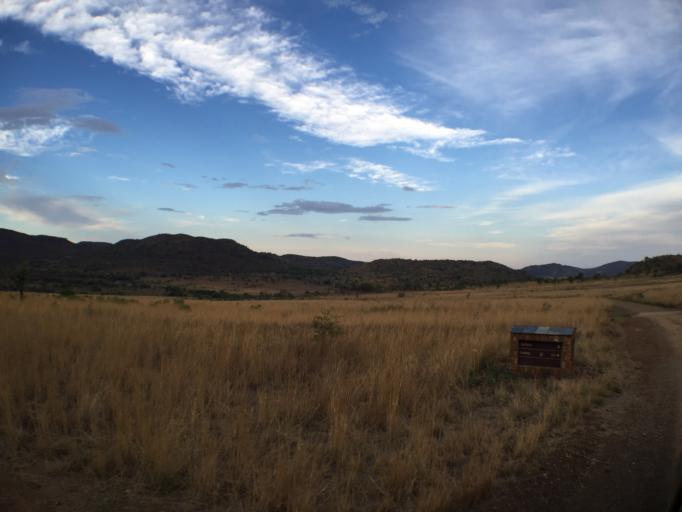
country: ZA
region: North-West
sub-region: Bojanala Platinum District Municipality
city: Mogwase
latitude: -25.2292
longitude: 27.0738
